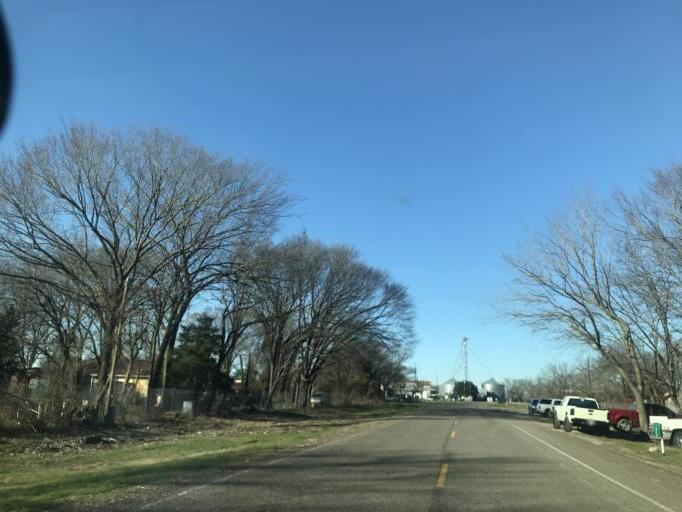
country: US
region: Texas
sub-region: Ellis County
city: Ferris
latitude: 32.4893
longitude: -96.6664
